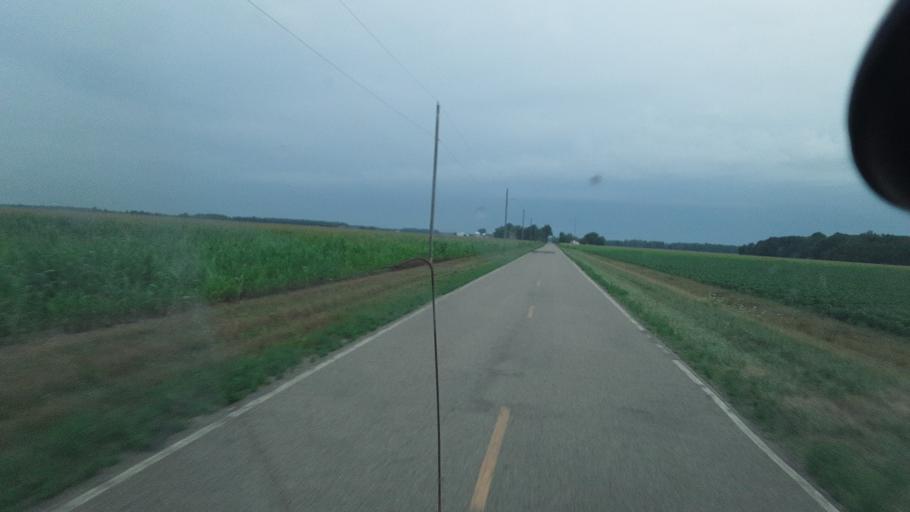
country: US
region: Ohio
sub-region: Defiance County
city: Hicksville
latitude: 41.2670
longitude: -84.7343
